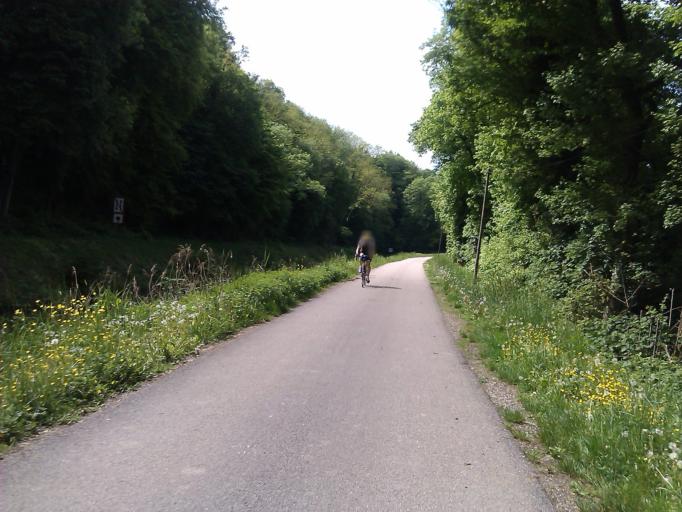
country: FR
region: Franche-Comte
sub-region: Departement du Doubs
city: Montferrand-le-Chateau
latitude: 47.1702
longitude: 5.9110
